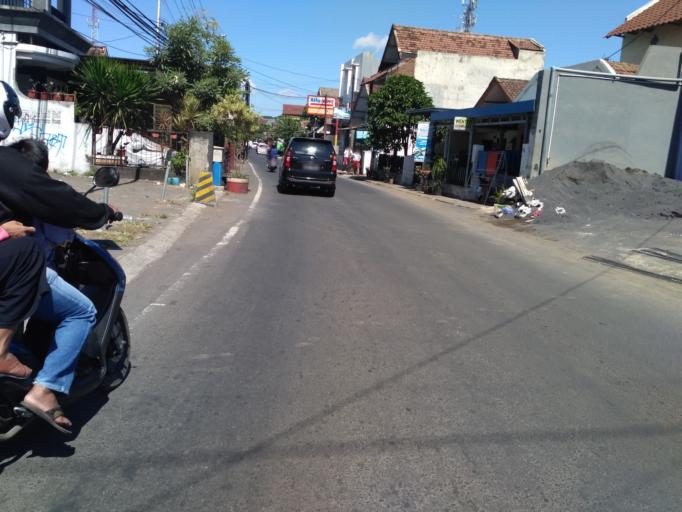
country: ID
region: East Java
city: Malang
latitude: -7.9856
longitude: 112.6460
